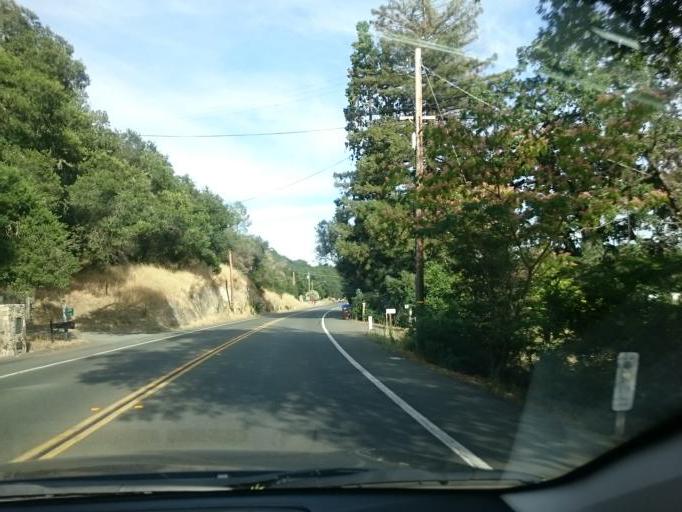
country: US
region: California
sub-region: Napa County
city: Saint Helena
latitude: 38.4982
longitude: -122.4262
